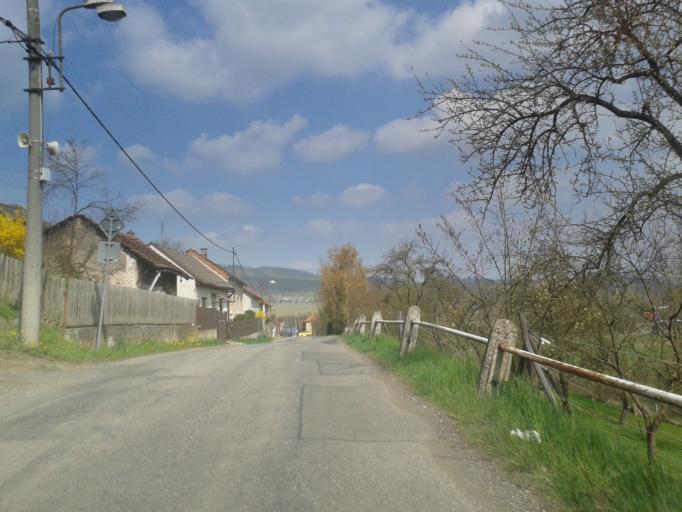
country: CZ
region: Central Bohemia
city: Zdice
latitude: 49.8965
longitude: 13.9607
